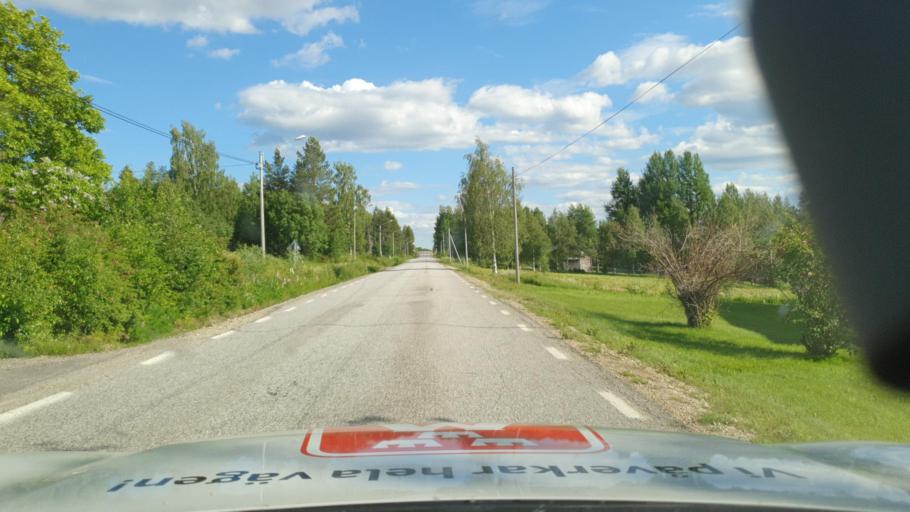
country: SE
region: Vaesterbotten
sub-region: Skelleftea Kommun
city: Langsele
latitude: 64.7512
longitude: 19.9417
